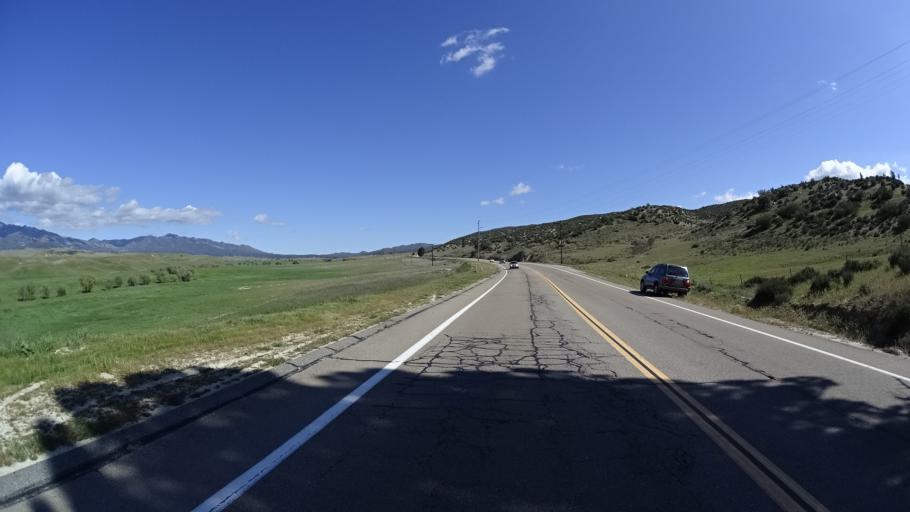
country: US
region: California
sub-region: San Diego County
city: Julian
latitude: 33.2399
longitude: -116.6589
